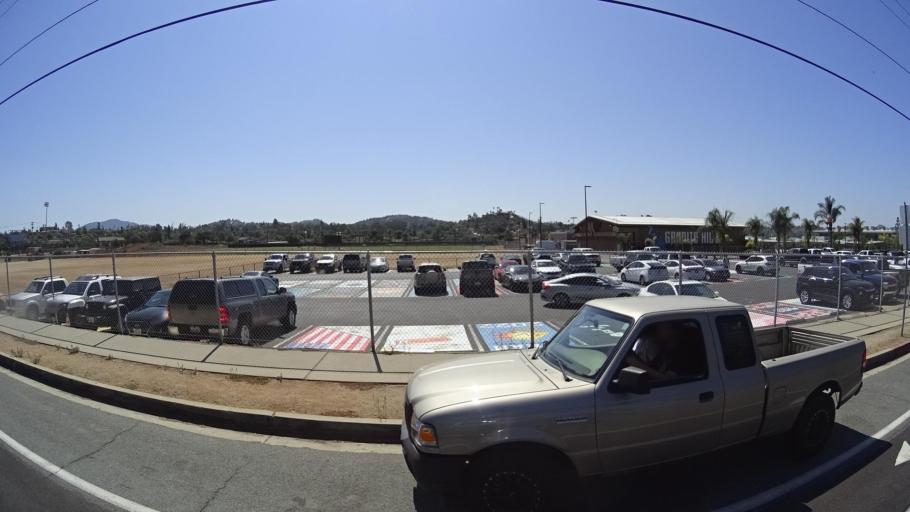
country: US
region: California
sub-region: San Diego County
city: Granite Hills
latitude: 32.8002
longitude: -116.9140
